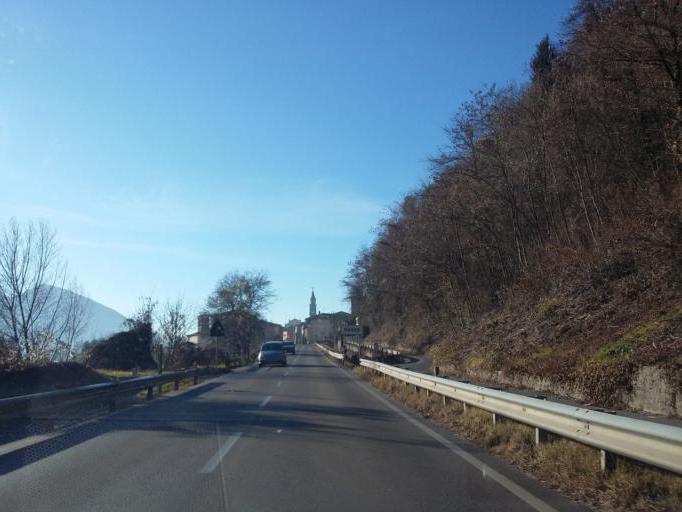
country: IT
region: Trentino-Alto Adige
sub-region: Provincia di Trento
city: Lodrone-Darzo
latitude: 45.8455
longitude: 10.5529
